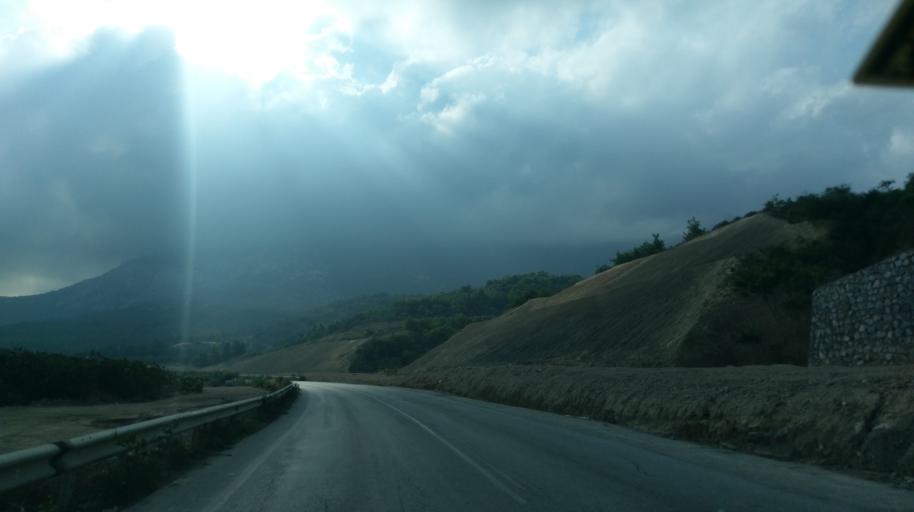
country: CY
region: Keryneia
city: Kyrenia
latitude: 35.3077
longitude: 33.4234
